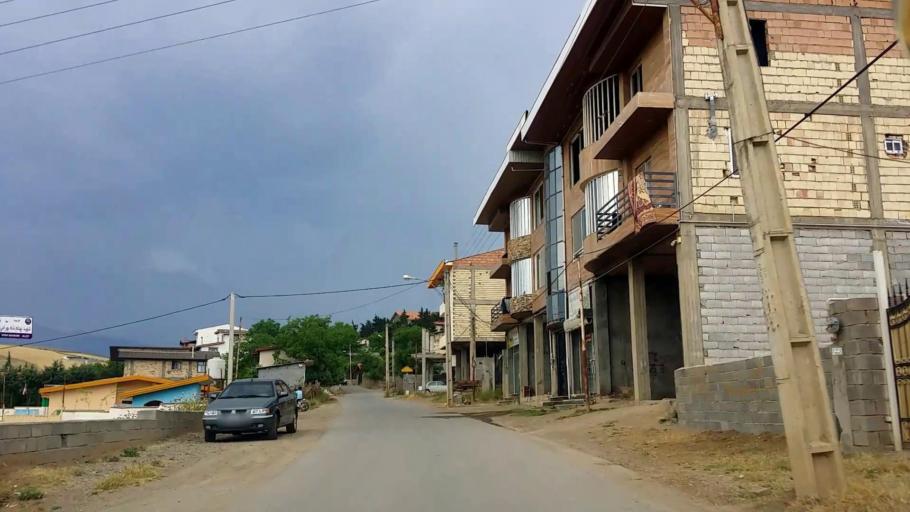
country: IR
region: Mazandaran
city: Chalus
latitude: 36.5151
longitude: 51.2528
